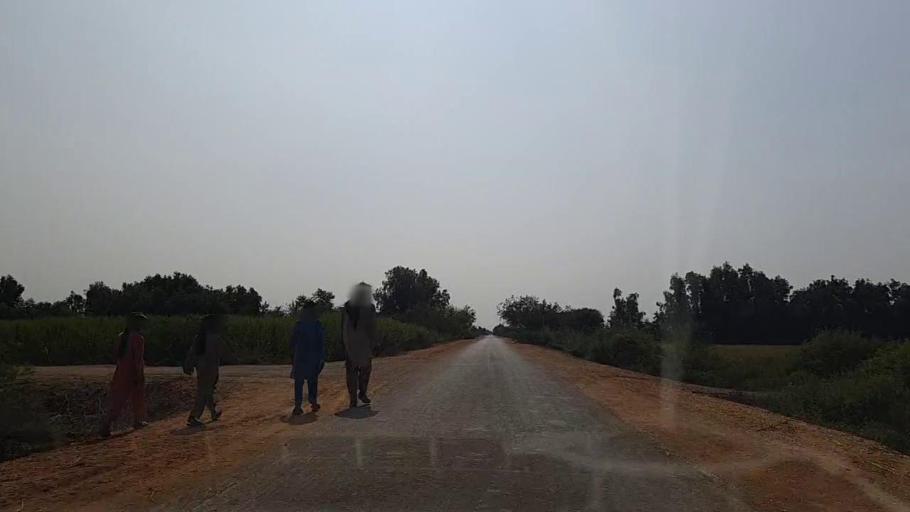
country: PK
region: Sindh
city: Chuhar Jamali
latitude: 24.2624
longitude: 67.9085
